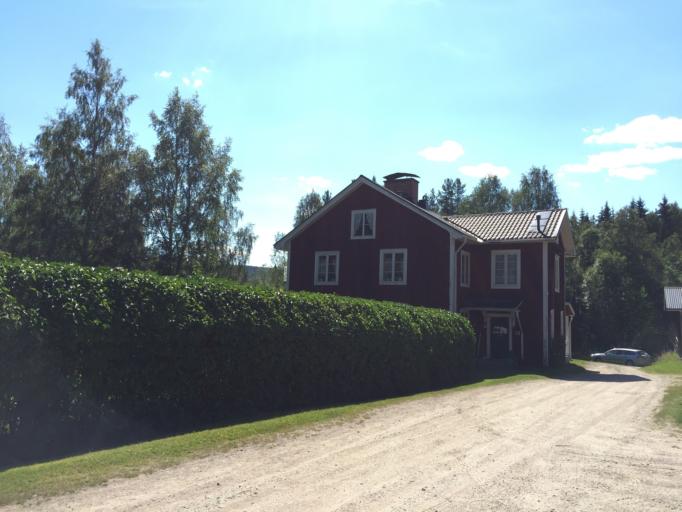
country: SE
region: Gaevleborg
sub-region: Ovanakers Kommun
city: Edsbyn
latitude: 61.3661
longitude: 15.4852
